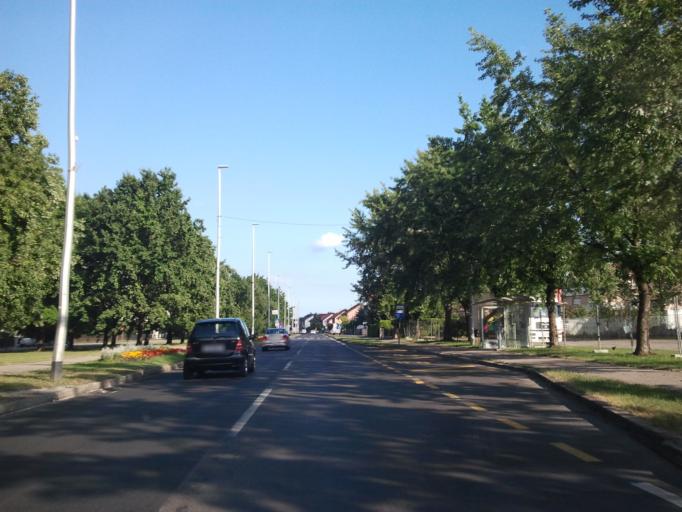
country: HR
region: Zagrebacka
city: Gradici
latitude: 45.7174
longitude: 16.0570
